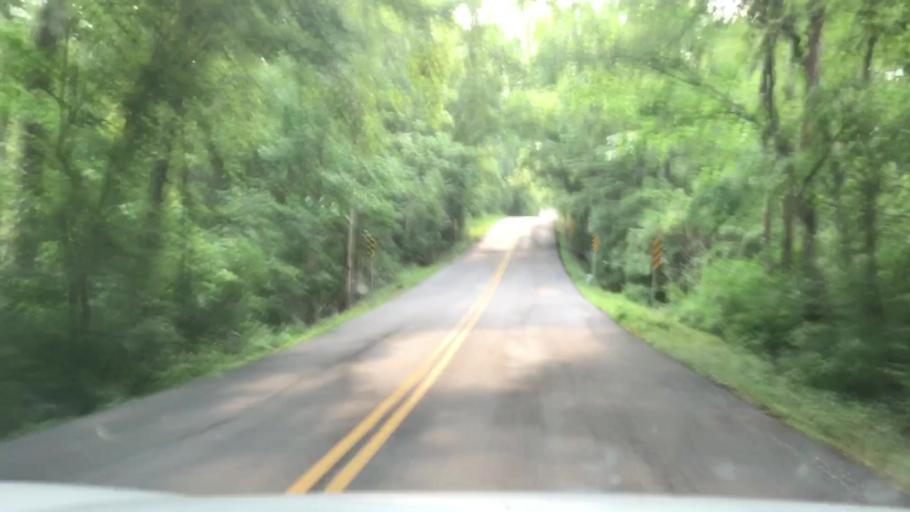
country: US
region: Missouri
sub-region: Saint Charles County
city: Cottleville
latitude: 38.7049
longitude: -90.6485
